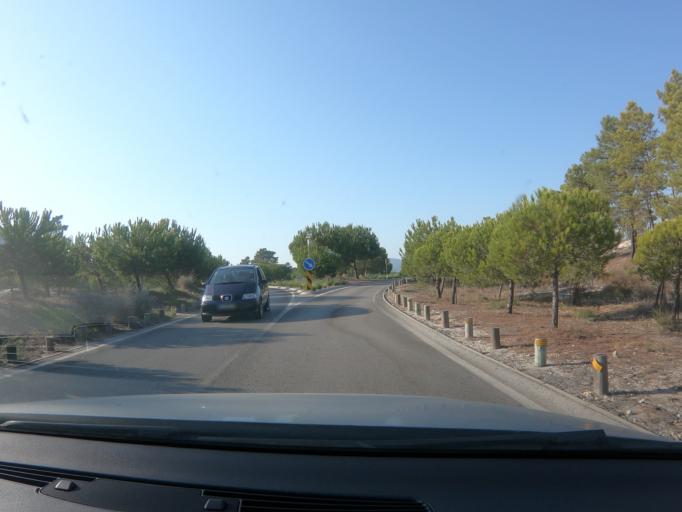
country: PT
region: Setubal
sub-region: Setubal
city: Setubal
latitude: 38.4746
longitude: -8.8857
